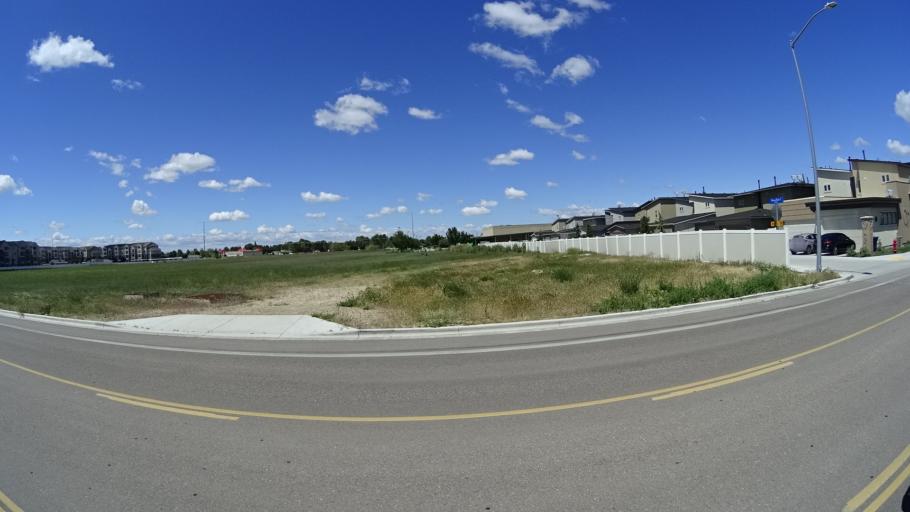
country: US
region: Idaho
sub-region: Ada County
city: Meridian
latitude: 43.6301
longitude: -116.3494
